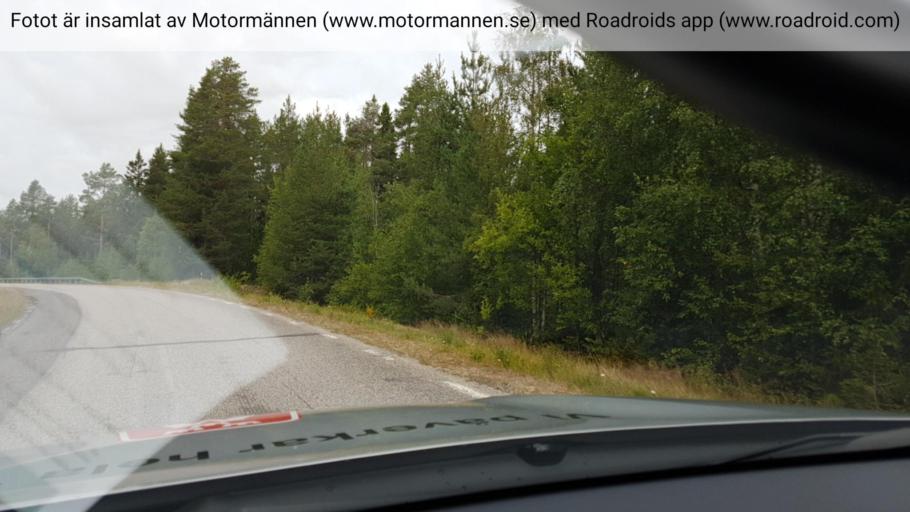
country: SE
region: Norrbotten
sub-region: Bodens Kommun
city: Saevast
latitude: 65.6714
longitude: 21.7009
